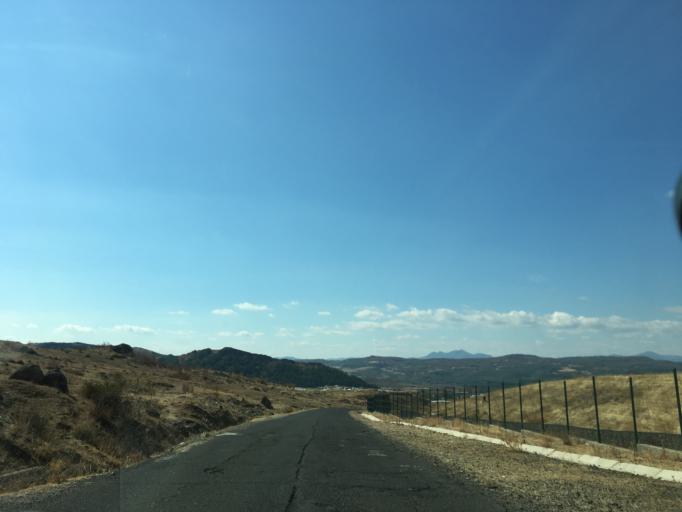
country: BG
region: Kurdzhali
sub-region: Obshtina Dzhebel
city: Dzhebel
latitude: 41.5220
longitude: 25.4341
